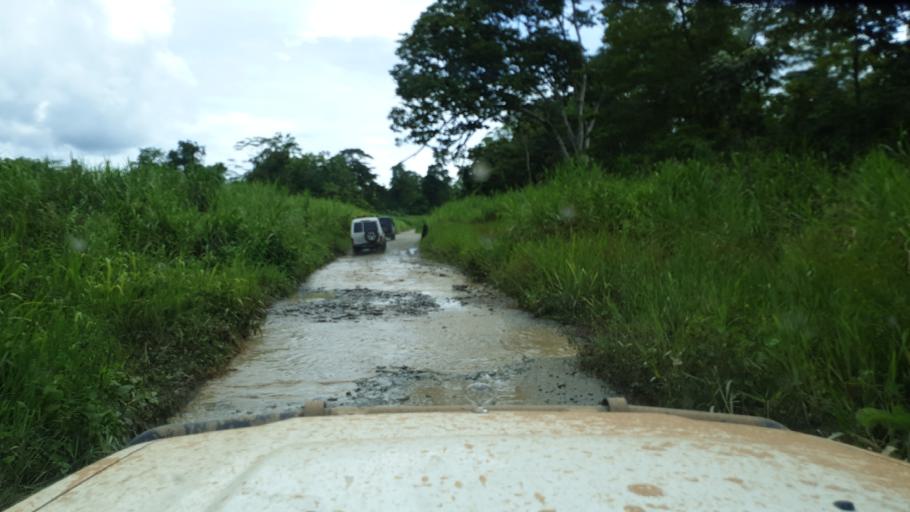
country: PG
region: Northern Province
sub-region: Sohe
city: Kokoda
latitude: -8.9164
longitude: 147.8562
